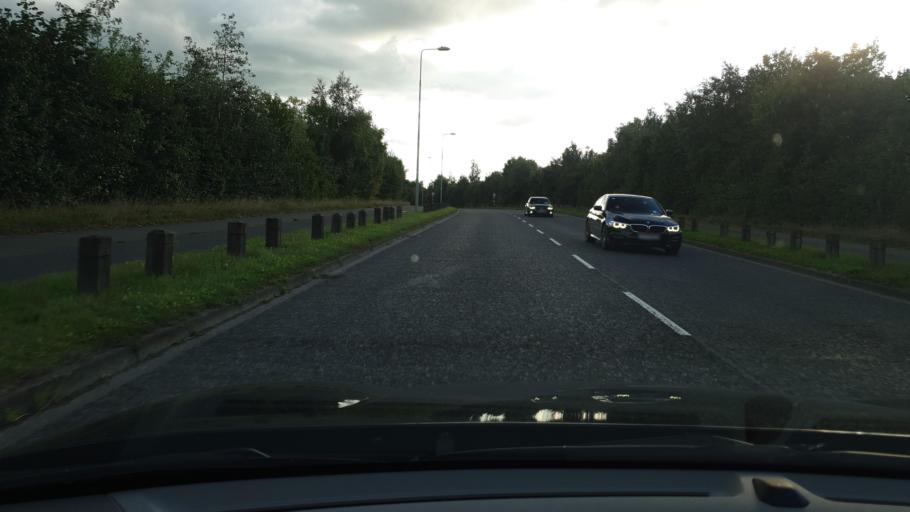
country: IE
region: Leinster
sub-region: Kildare
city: Naas
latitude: 53.2197
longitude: -6.6973
